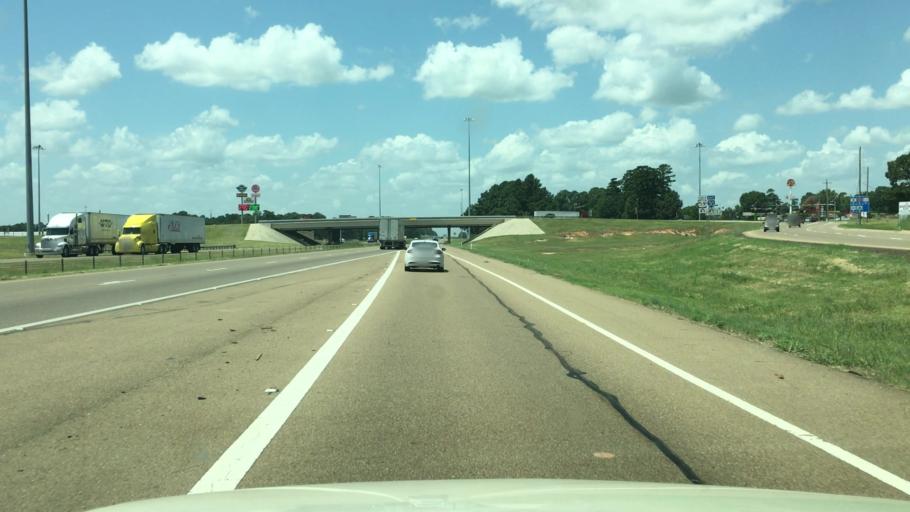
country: US
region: Texas
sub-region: Bowie County
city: Nash
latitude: 33.4540
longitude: -94.1275
